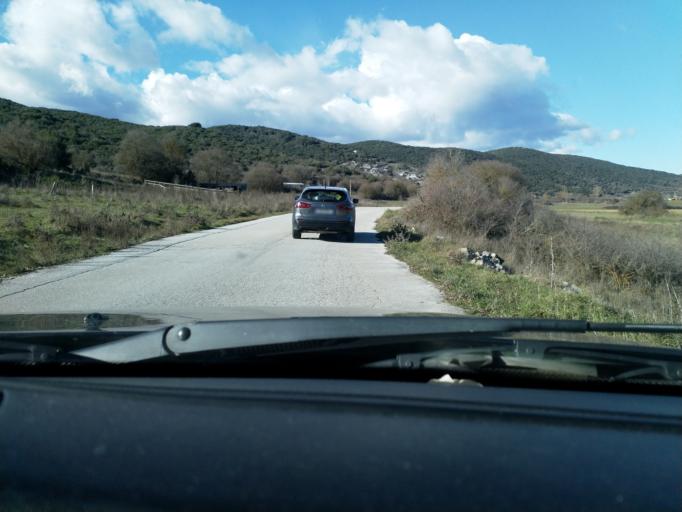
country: GR
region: Epirus
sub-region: Nomos Ioanninon
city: Kalpaki
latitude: 39.8758
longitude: 20.6846
